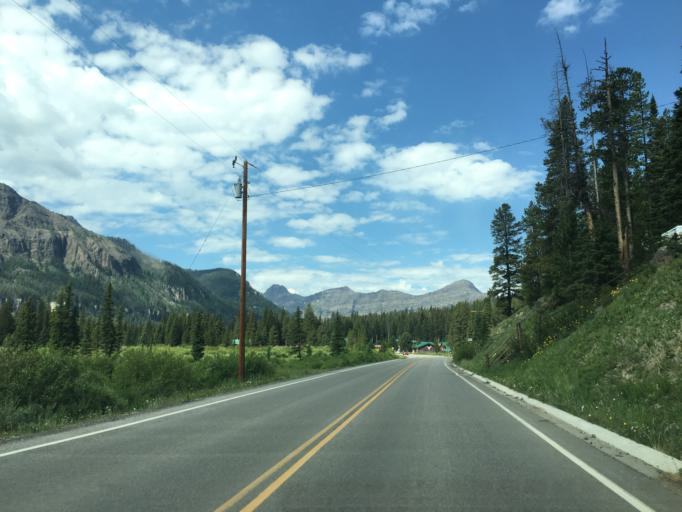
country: US
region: Montana
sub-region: Stillwater County
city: Absarokee
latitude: 45.0081
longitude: -109.9847
